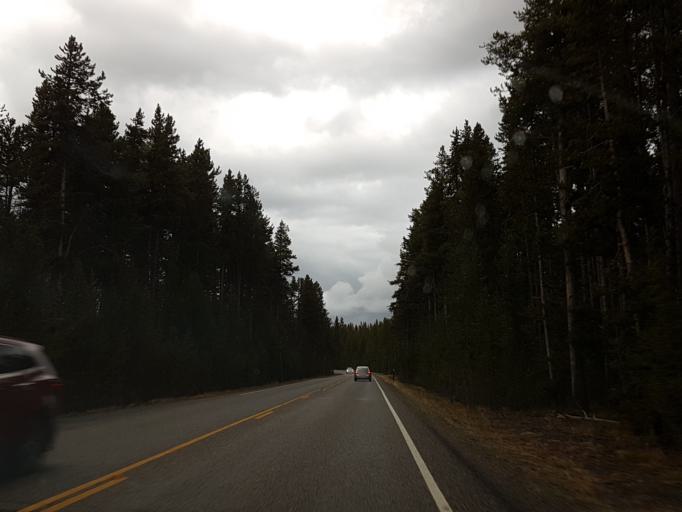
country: US
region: Montana
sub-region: Gallatin County
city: West Yellowstone
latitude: 44.4573
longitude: -110.5085
